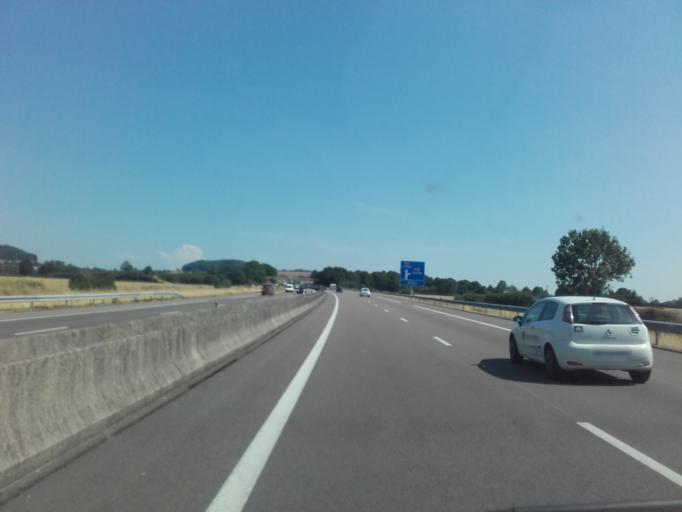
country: FR
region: Bourgogne
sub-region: Departement de la Cote-d'Or
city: Pouilly-en-Auxois
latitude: 47.2619
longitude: 4.5216
